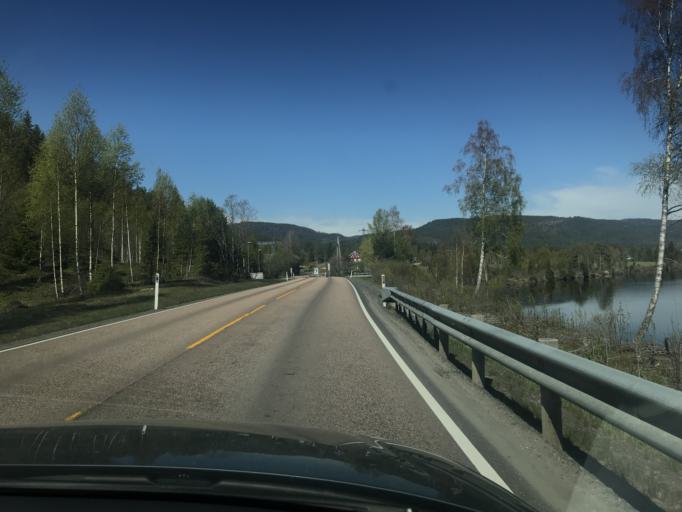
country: NO
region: Buskerud
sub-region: Kongsberg
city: Kongsberg
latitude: 59.7002
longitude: 9.6165
